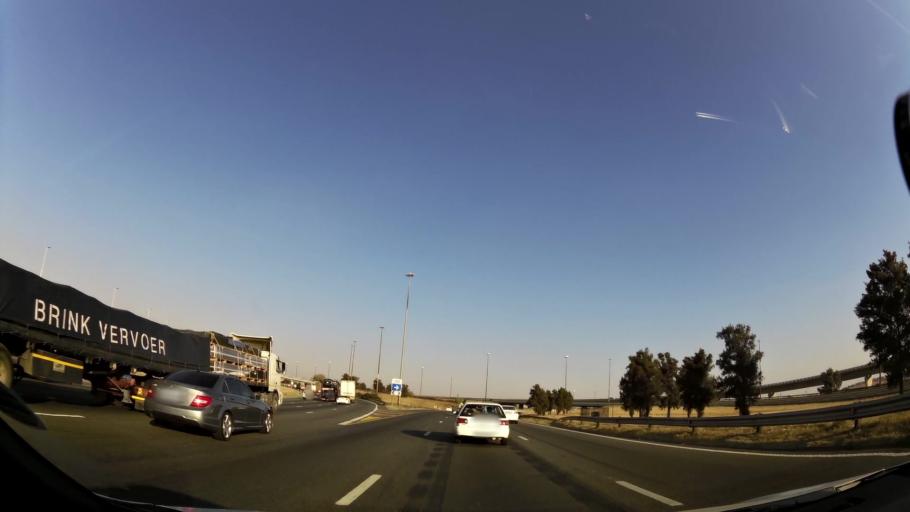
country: ZA
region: Gauteng
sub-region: Ekurhuleni Metropolitan Municipality
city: Germiston
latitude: -26.2366
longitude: 28.1251
